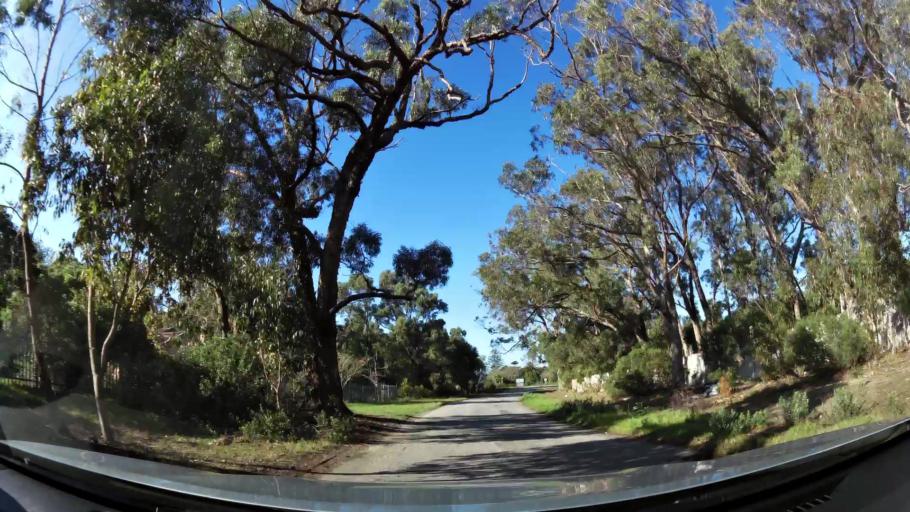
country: ZA
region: Eastern Cape
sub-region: Nelson Mandela Bay Metropolitan Municipality
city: Port Elizabeth
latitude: -33.9853
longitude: 25.6331
